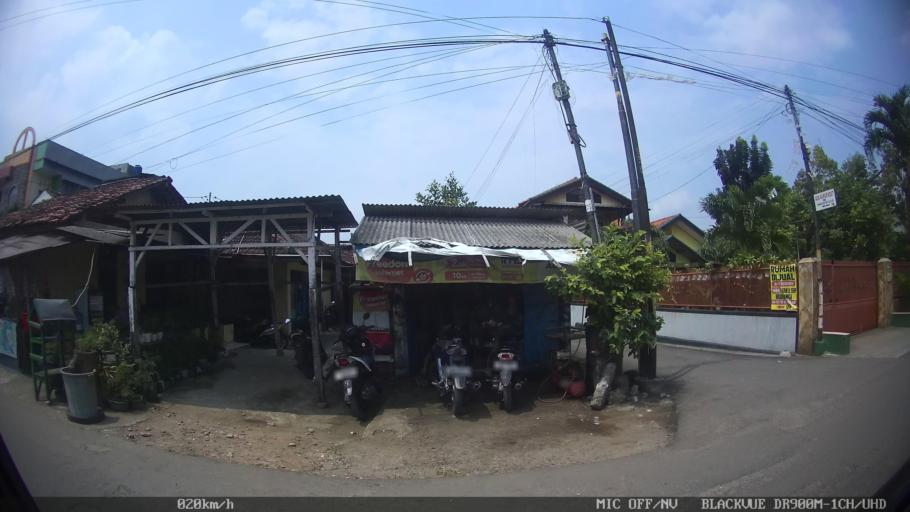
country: ID
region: Lampung
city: Bandarlampung
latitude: -5.4342
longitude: 105.2662
